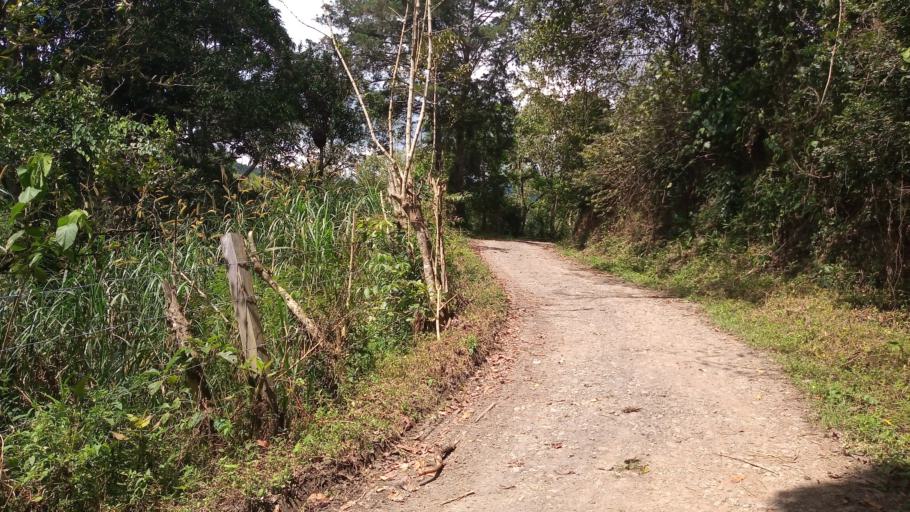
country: CO
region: Boyaca
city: Garagoa
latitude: 5.0788
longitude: -73.3835
